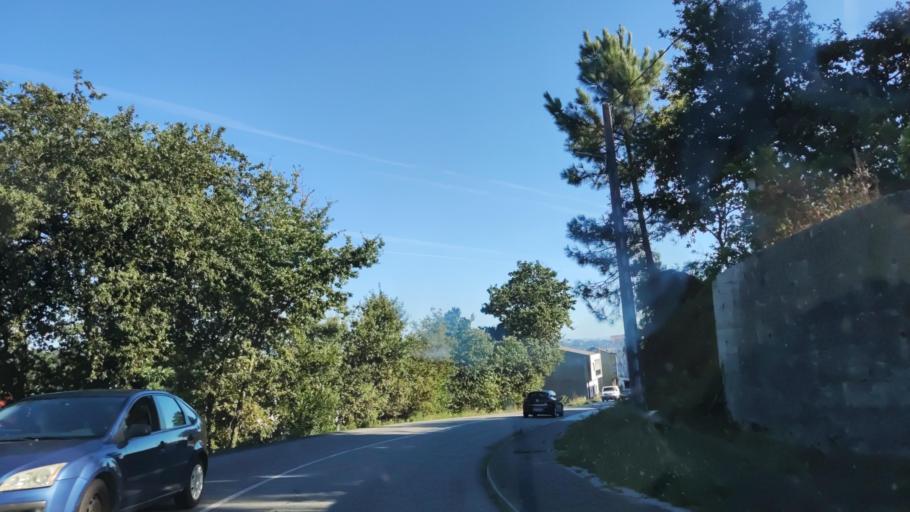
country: ES
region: Galicia
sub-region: Provincia da Coruna
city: Boiro
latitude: 42.6536
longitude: -8.8799
